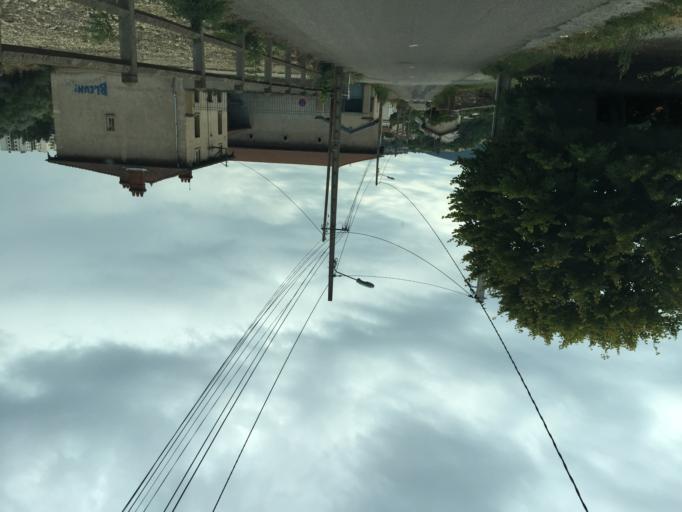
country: FR
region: Rhone-Alpes
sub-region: Departement de la Loire
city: Saint-Chamond
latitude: 45.4802
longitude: 4.5406
